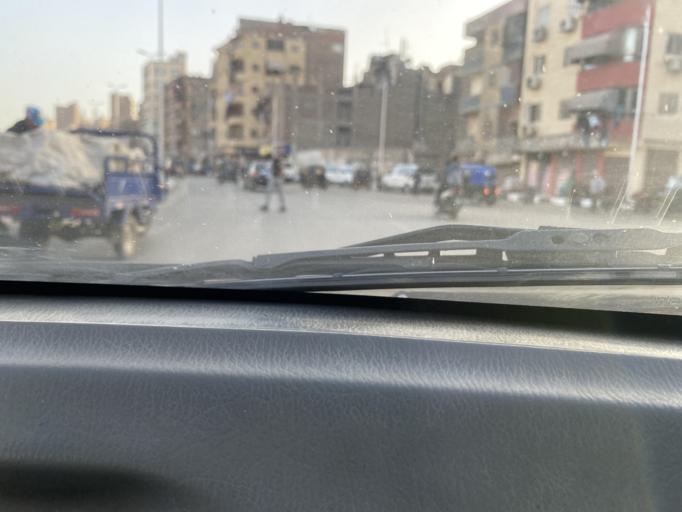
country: EG
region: Muhafazat al Qahirah
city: Cairo
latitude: 30.1253
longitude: 31.2974
